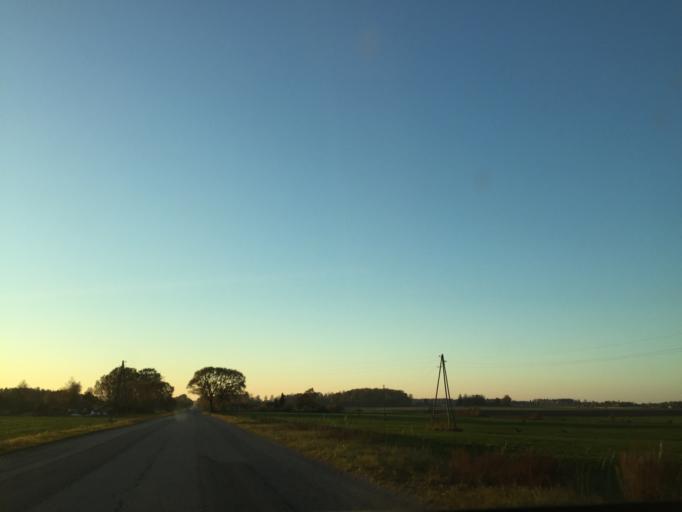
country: LT
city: Vieksniai
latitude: 56.4024
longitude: 22.5312
